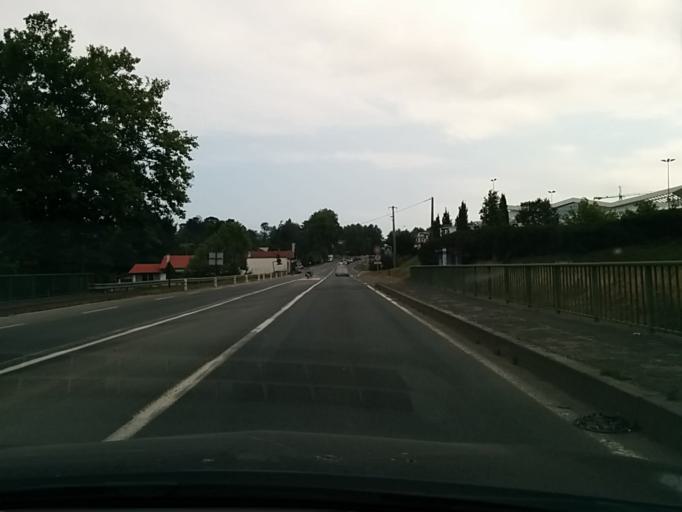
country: FR
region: Aquitaine
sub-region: Departement des Pyrenees-Atlantiques
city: Ciboure
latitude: 43.3729
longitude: -1.6805
